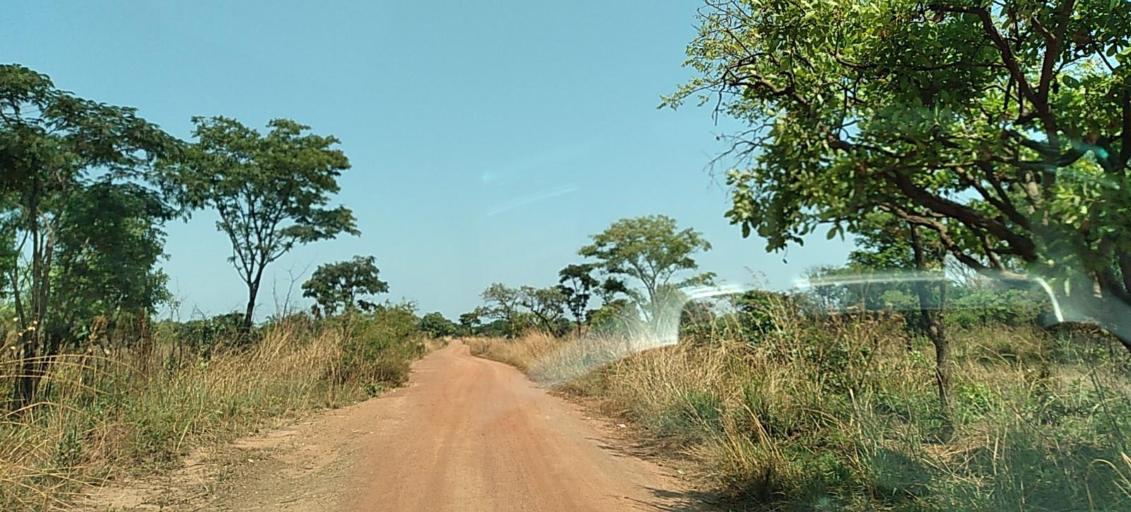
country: ZM
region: Copperbelt
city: Chingola
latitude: -12.5434
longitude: 27.7440
